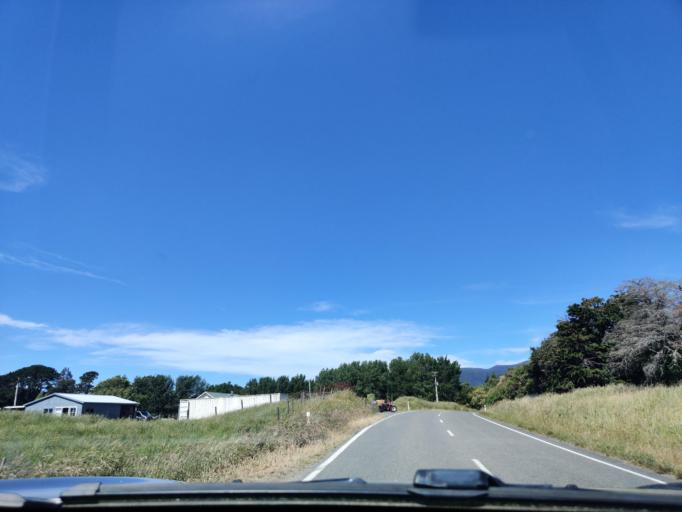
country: NZ
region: Wellington
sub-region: Upper Hutt City
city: Upper Hutt
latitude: -41.3269
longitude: 175.2275
